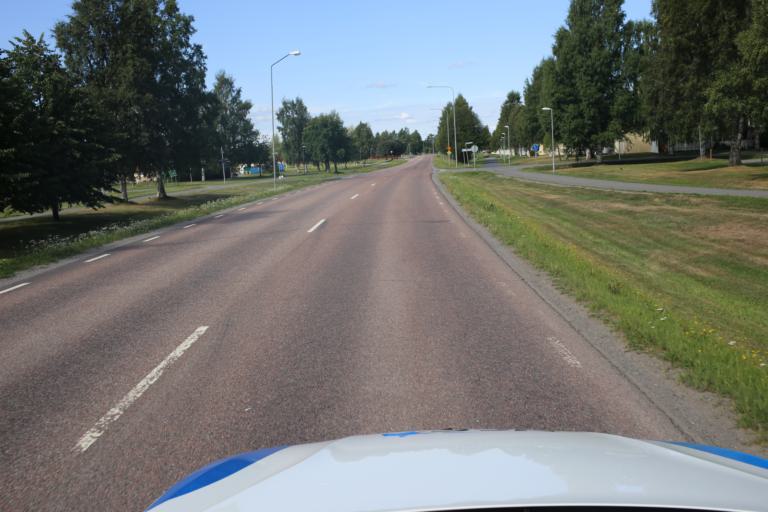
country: SE
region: Vaesterbotten
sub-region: Skelleftea Kommun
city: Skelleftea
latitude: 64.7449
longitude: 20.9844
